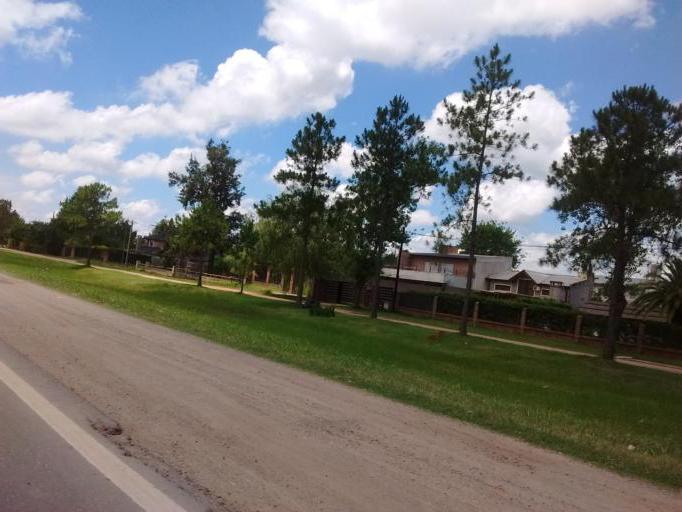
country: AR
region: Santa Fe
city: Funes
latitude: -32.9233
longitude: -60.7946
